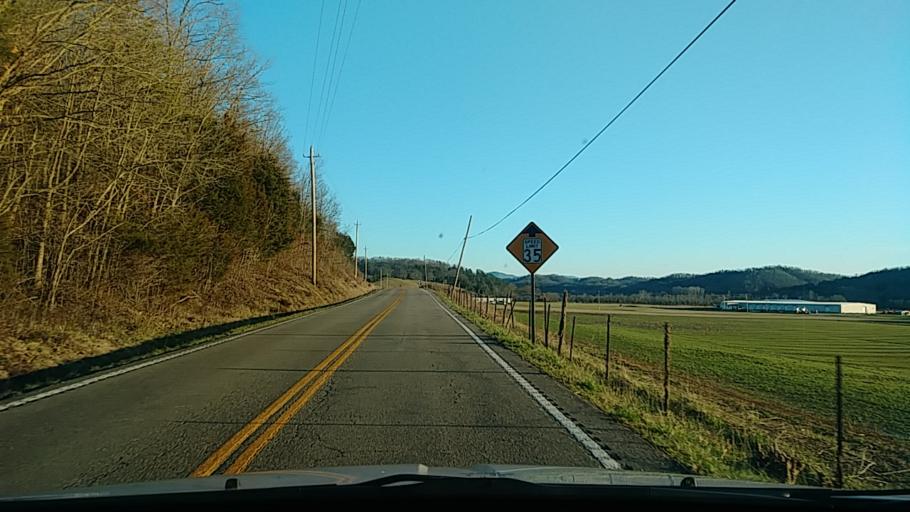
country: US
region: Tennessee
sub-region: Greene County
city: Mosheim
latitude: 36.1162
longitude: -83.0803
